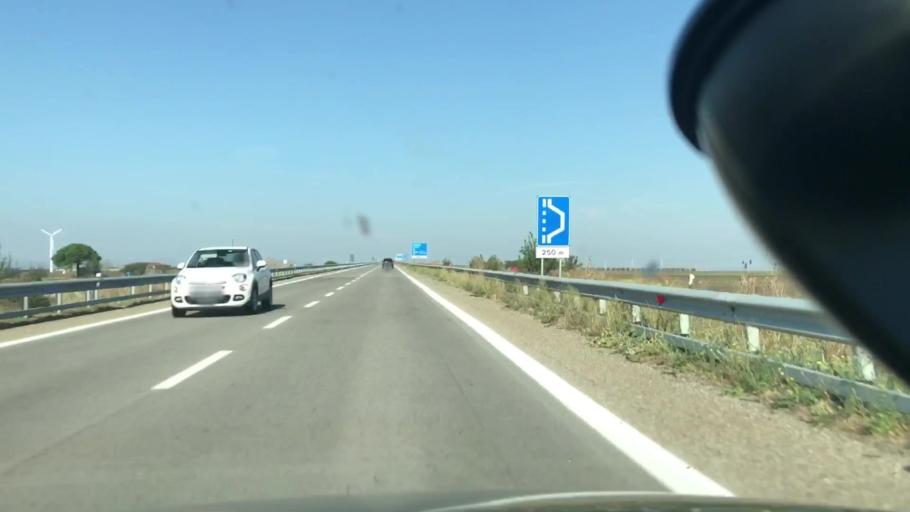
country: IT
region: Basilicate
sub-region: Provincia di Potenza
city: Montemilone
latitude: 40.9909
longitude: 15.8979
